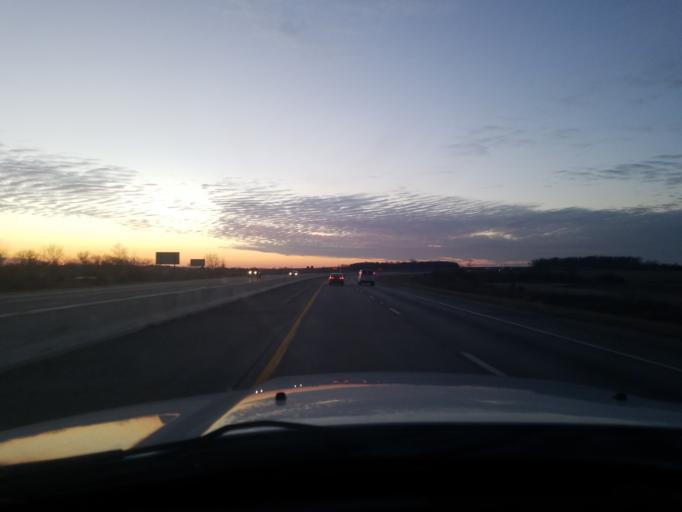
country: US
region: Indiana
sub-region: Wells County
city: Ossian
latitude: 40.9518
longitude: -85.2458
